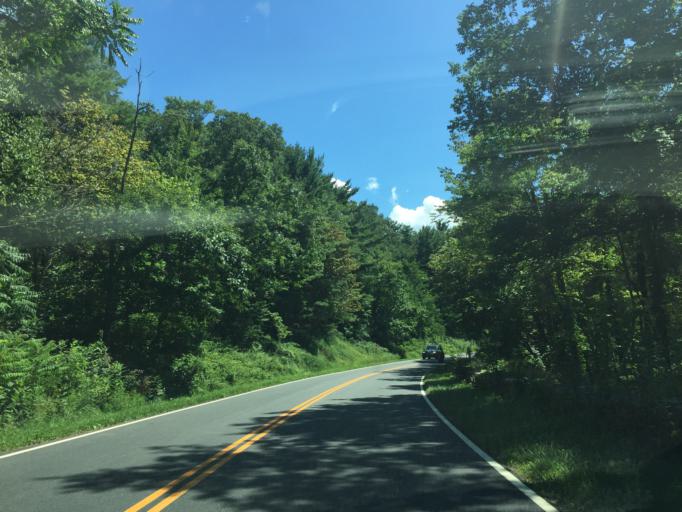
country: US
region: Virginia
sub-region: Rappahannock County
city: Washington
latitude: 38.7425
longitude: -78.3058
